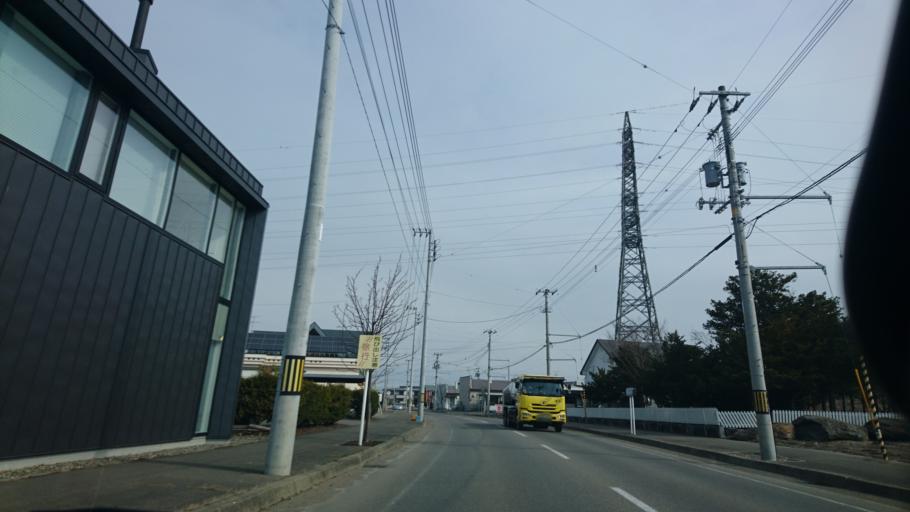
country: JP
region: Hokkaido
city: Otofuke
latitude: 42.9636
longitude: 143.2132
